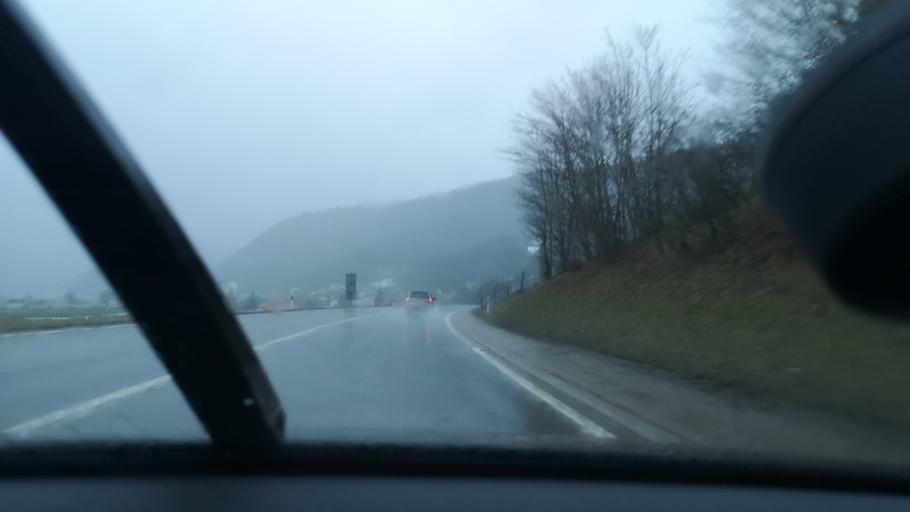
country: CH
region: Neuchatel
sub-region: Val-de-Travers District
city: Couvet
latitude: 46.9192
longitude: 6.6109
